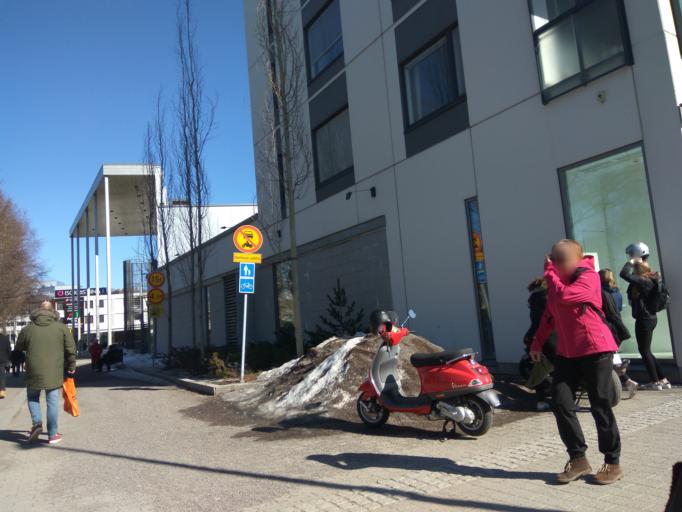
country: FI
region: South Karelia
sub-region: Lappeenranta
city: Lappeenranta
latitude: 61.0559
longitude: 28.1884
